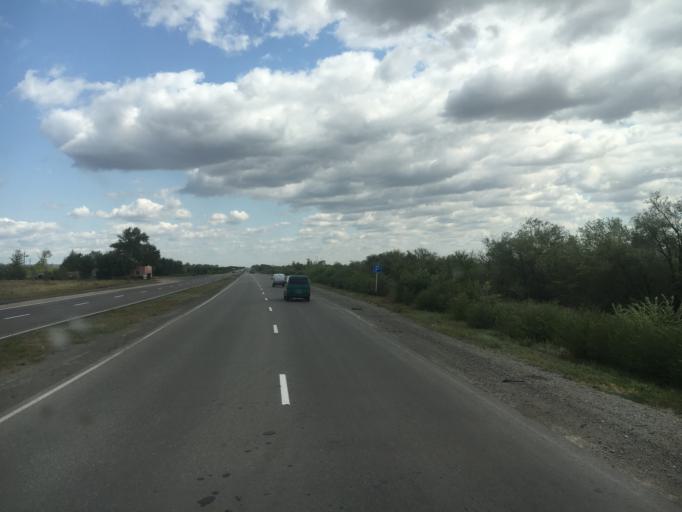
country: KZ
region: Qostanay
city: Rudnyy
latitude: 52.9896
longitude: 63.2476
